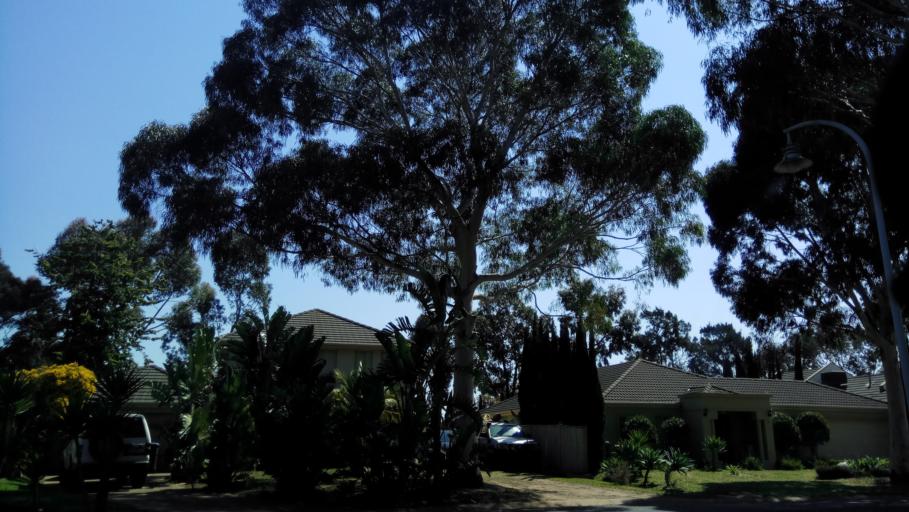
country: AU
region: Victoria
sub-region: Wyndham
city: Point Cook
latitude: -37.8960
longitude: 144.7552
